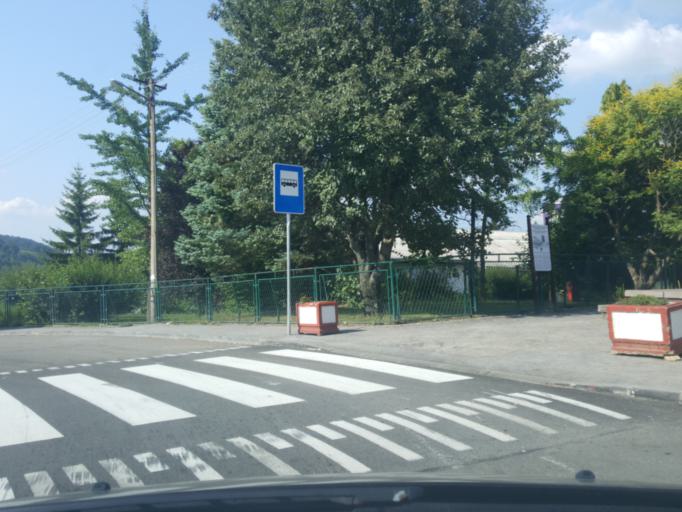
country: RS
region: Central Serbia
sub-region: Moravicki Okrug
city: Gornji Milanovac
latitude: 44.1408
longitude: 20.4989
